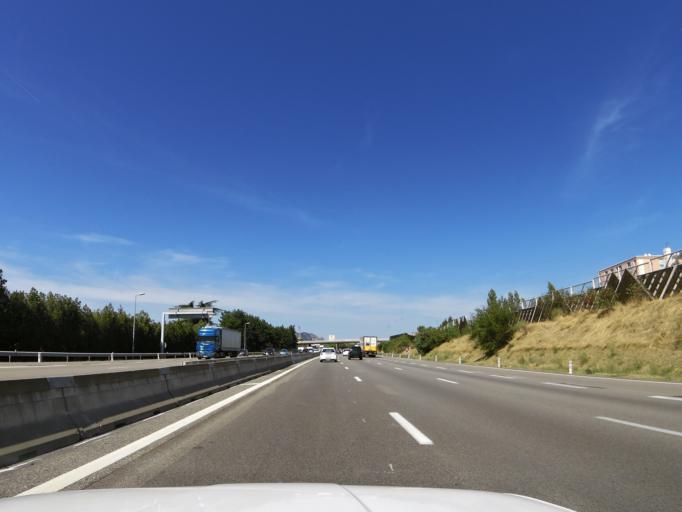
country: FR
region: Rhone-Alpes
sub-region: Departement de la Drome
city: Portes-les-Valence
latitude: 44.8689
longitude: 4.8651
